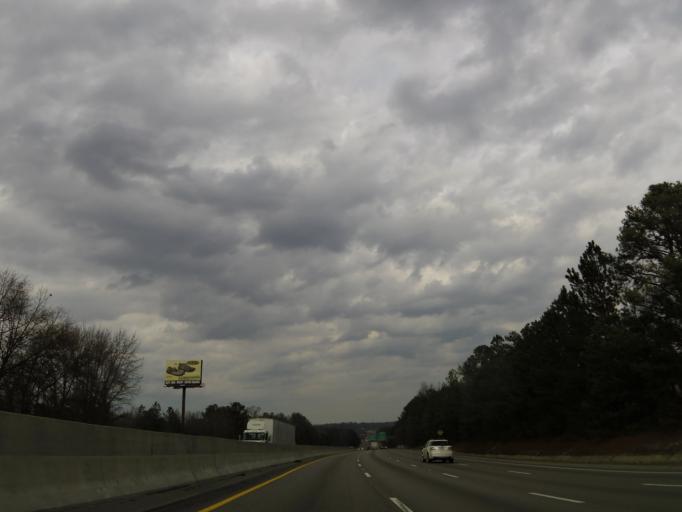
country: US
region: South Carolina
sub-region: Lexington County
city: West Columbia
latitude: 34.0096
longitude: -81.1105
